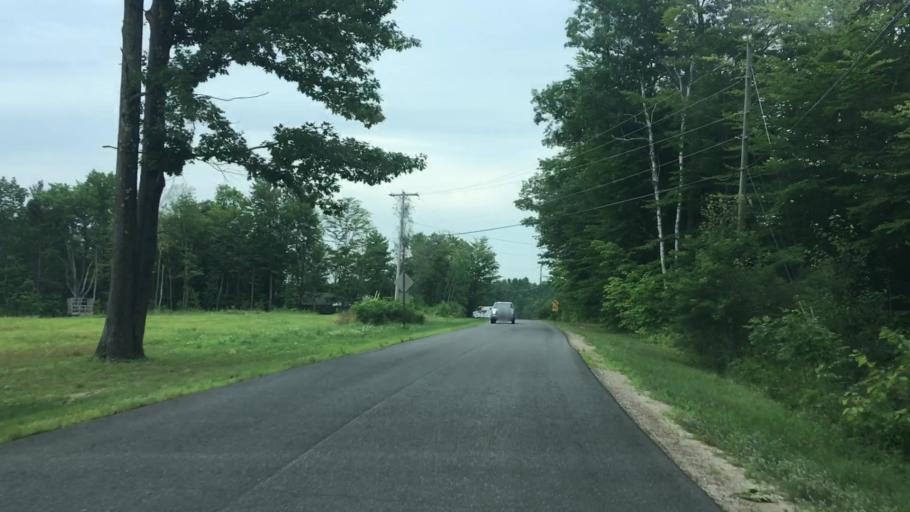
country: US
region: New York
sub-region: Clinton County
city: Peru
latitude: 44.6048
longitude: -73.6206
